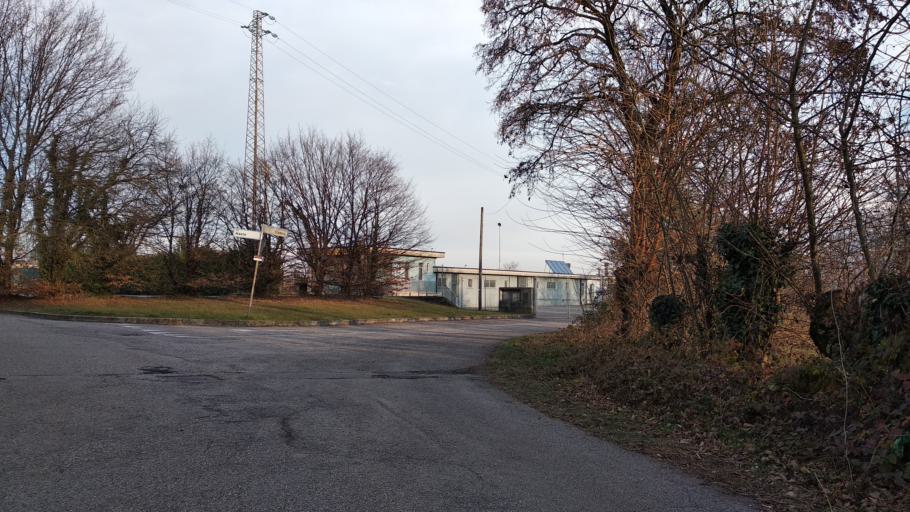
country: IT
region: Veneto
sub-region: Provincia di Vicenza
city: Schio
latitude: 45.7013
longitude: 11.3525
